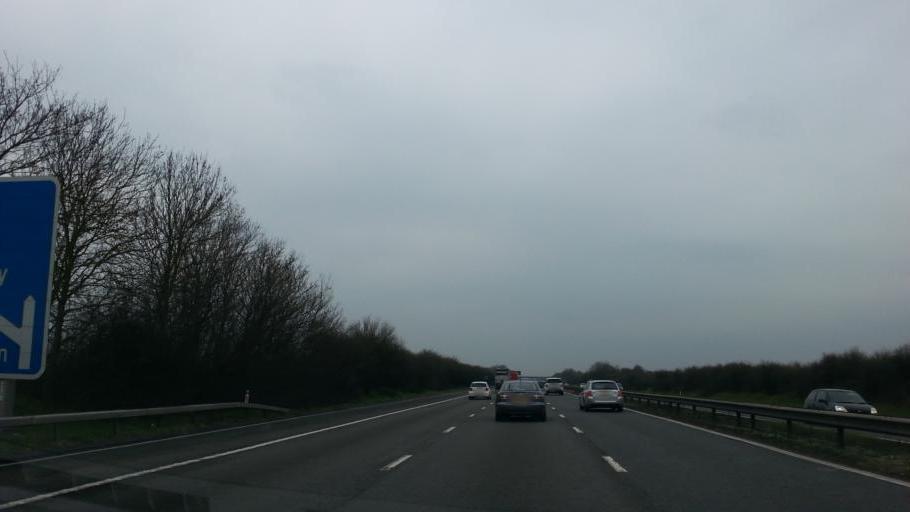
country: GB
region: England
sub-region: Gloucestershire
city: Tewkesbury
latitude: 51.9769
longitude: -2.1270
